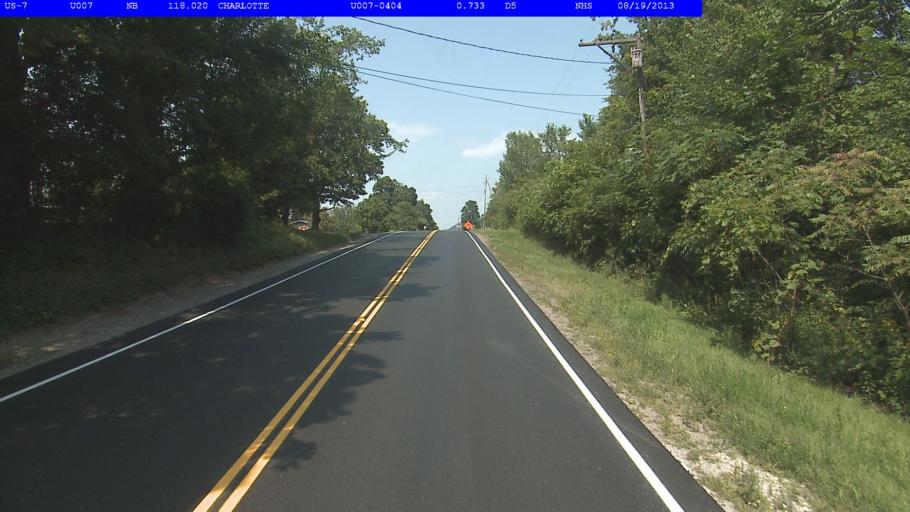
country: US
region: Vermont
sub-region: Addison County
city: Vergennes
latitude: 44.2728
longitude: -73.2339
